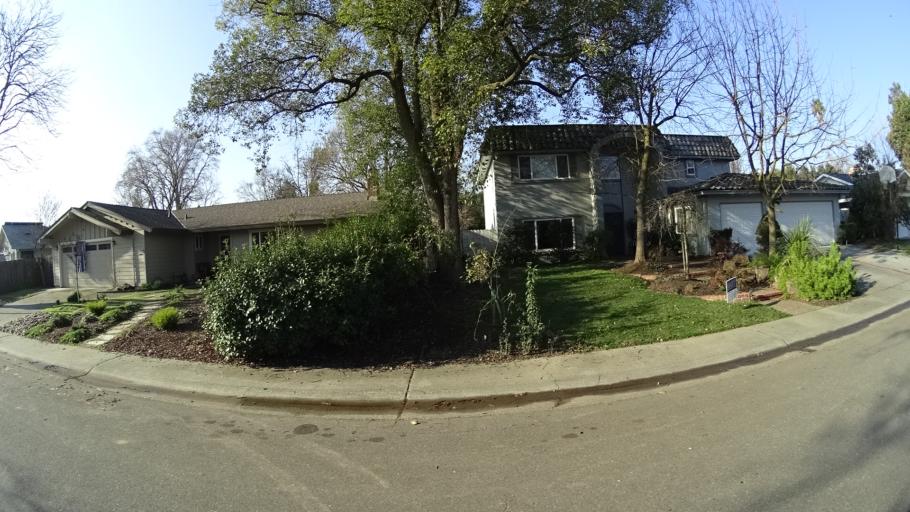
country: US
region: California
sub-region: Yolo County
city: Davis
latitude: 38.5480
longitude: -121.7927
